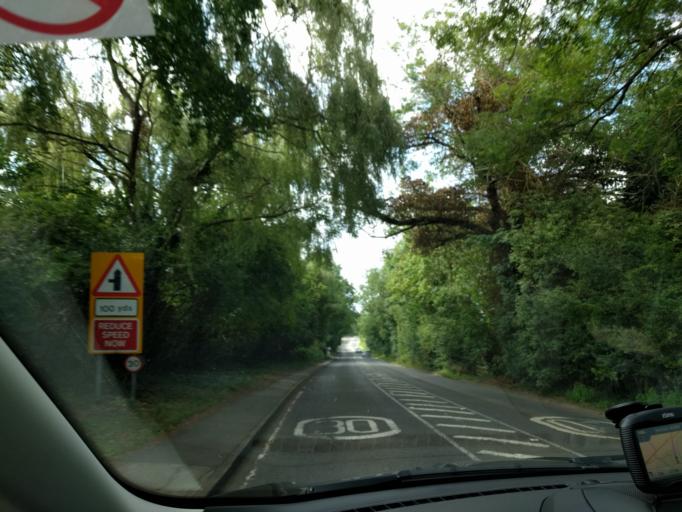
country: GB
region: England
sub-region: Warwickshire
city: Shipston on Stour
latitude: 52.0925
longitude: -1.6276
